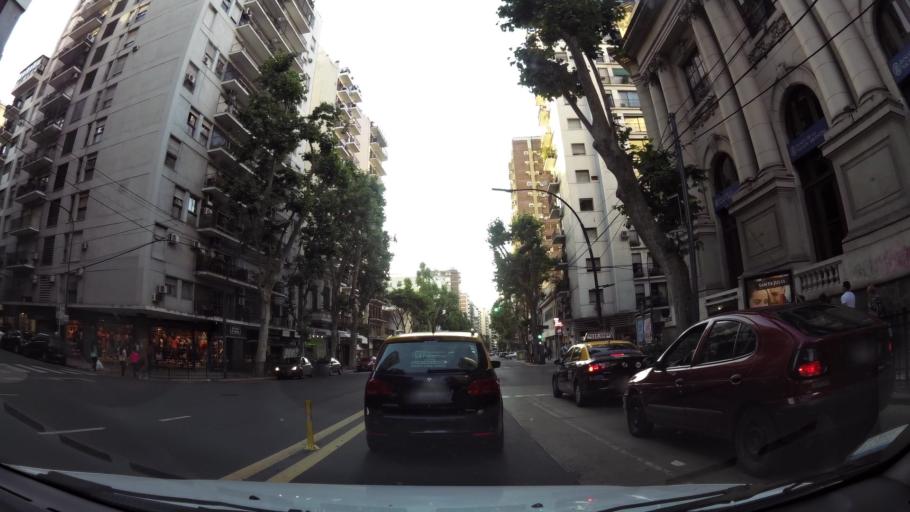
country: AR
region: Buenos Aires F.D.
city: Retiro
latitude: -34.5952
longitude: -58.3996
